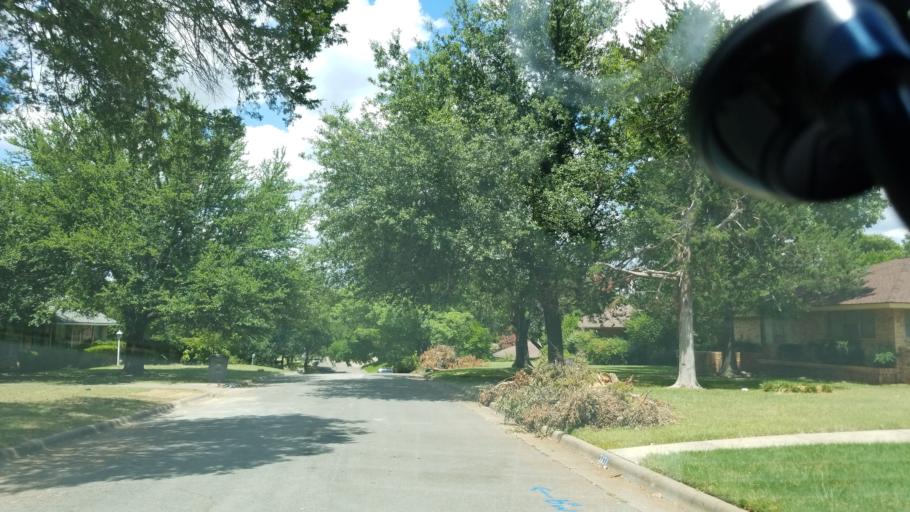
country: US
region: Texas
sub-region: Dallas County
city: Cockrell Hill
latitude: 32.7021
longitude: -96.8767
